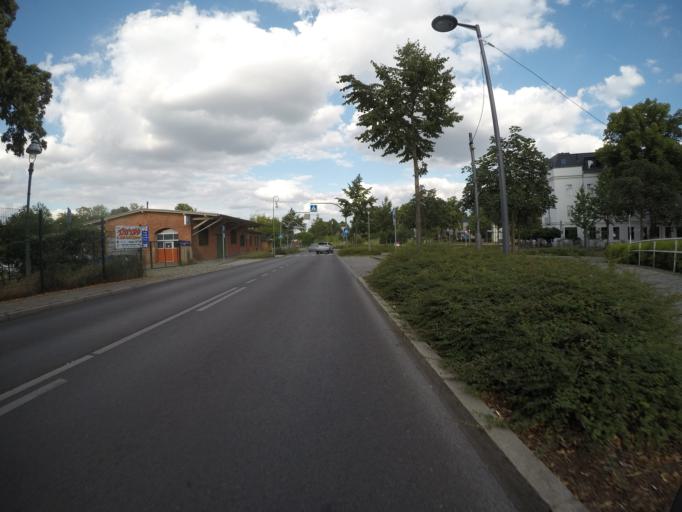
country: DE
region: Berlin
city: Kaulsdorf
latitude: 52.5117
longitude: 13.5864
